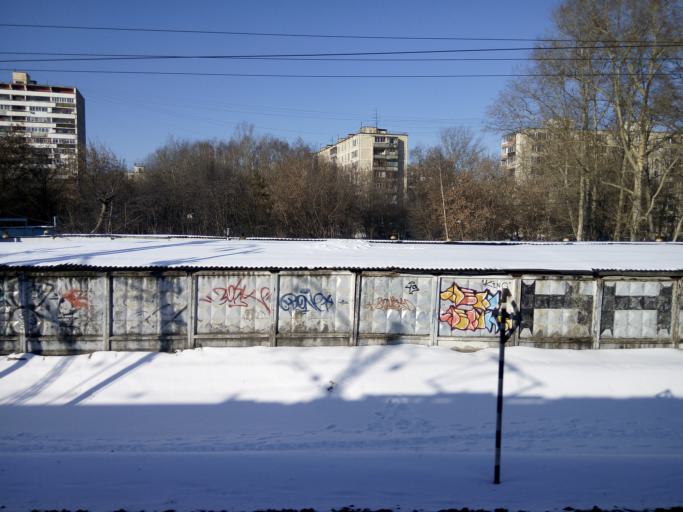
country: RU
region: Moscow
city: Slobodka
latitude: 55.8593
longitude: 37.5740
